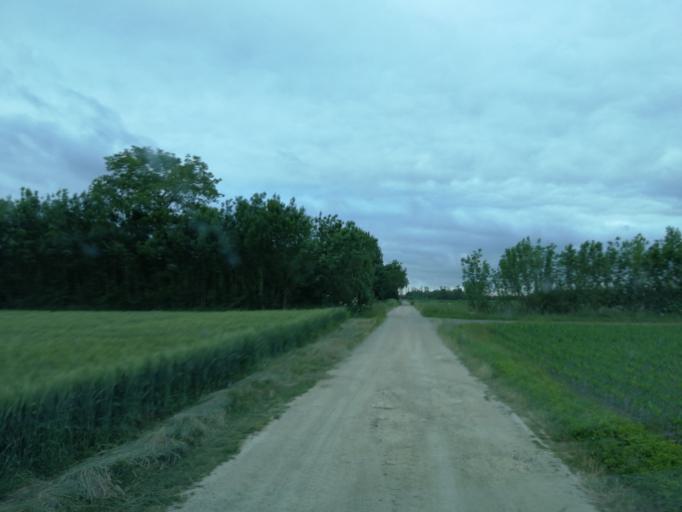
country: FR
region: Poitou-Charentes
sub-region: Departement de la Charente-Maritime
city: Marans
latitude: 46.3620
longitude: -0.9522
